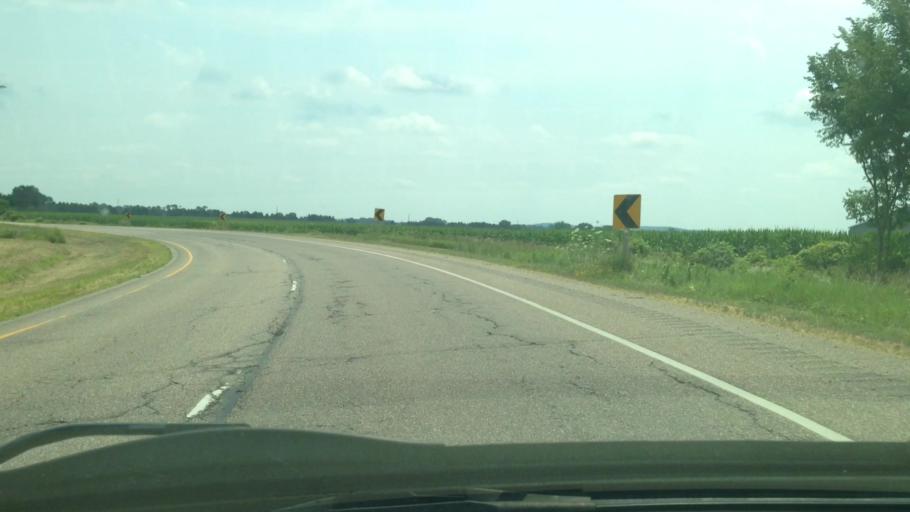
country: US
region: Wisconsin
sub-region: Sauk County
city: Prairie du Sac
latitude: 43.3514
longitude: -89.7668
